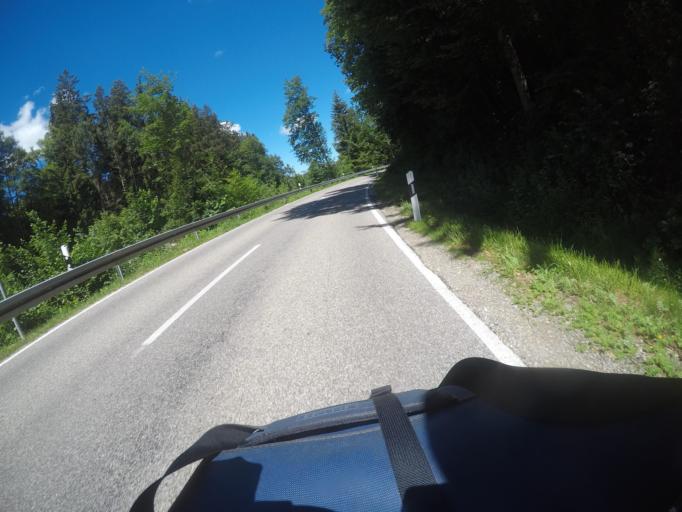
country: DE
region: Bavaria
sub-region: Upper Bavaria
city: Prem
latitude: 47.6547
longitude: 10.7872
